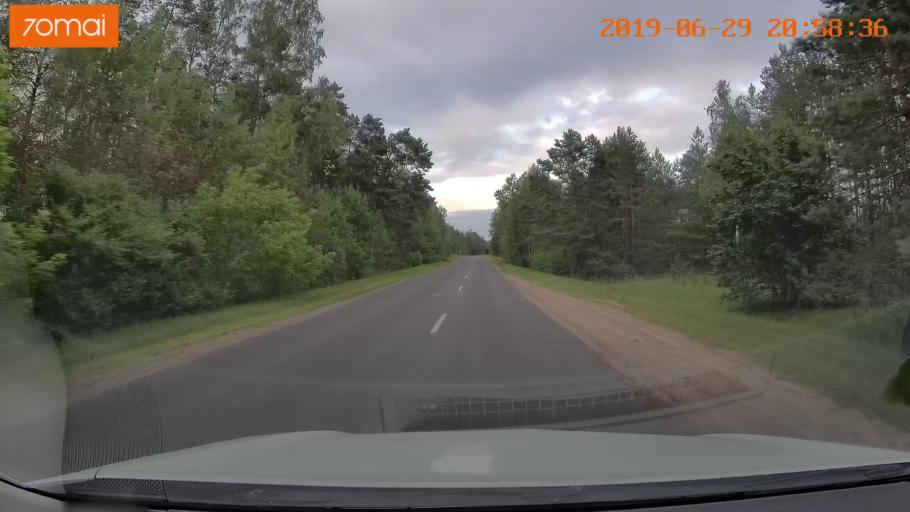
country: BY
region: Brest
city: Hantsavichy
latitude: 52.7312
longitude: 26.3894
